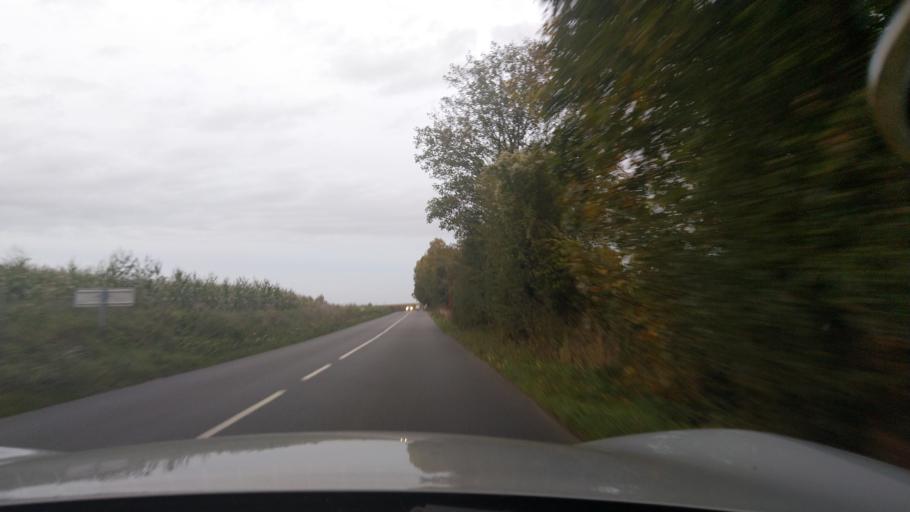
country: FR
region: Ile-de-France
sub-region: Departement de Seine-et-Marne
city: Claye-Souilly
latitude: 48.9663
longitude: 2.6830
